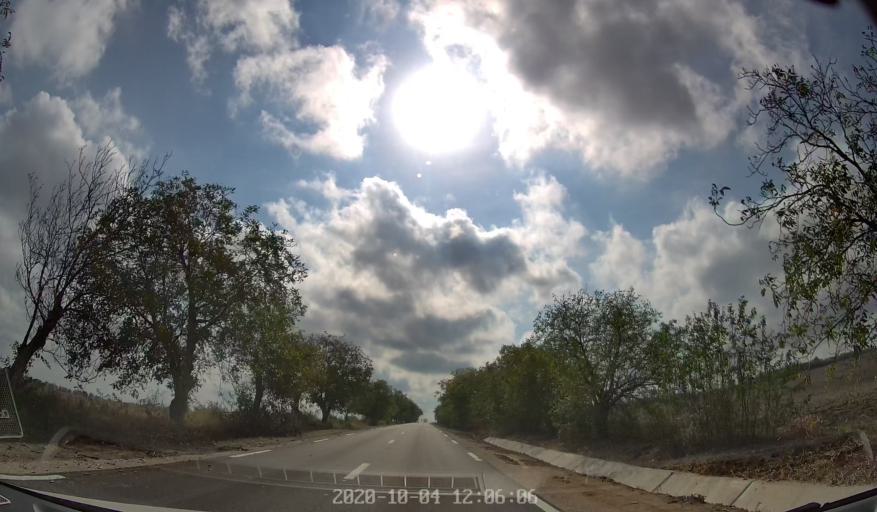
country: MD
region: Rezina
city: Saharna
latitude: 47.5866
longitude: 28.9549
